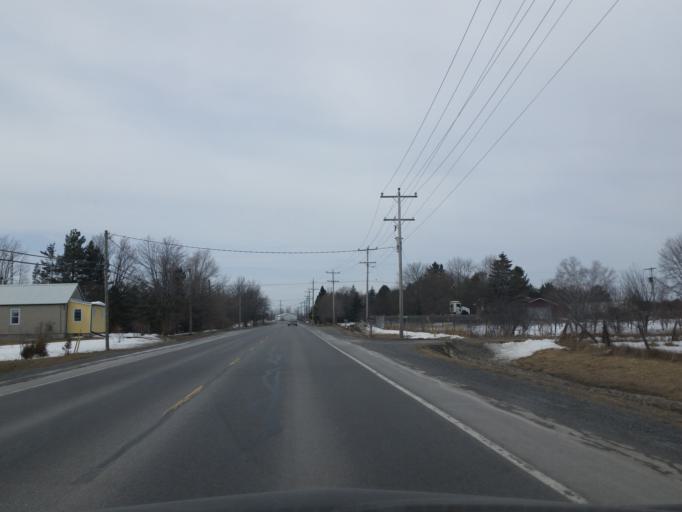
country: CA
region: Ontario
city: Skatepark
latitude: 44.2743
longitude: -76.7406
